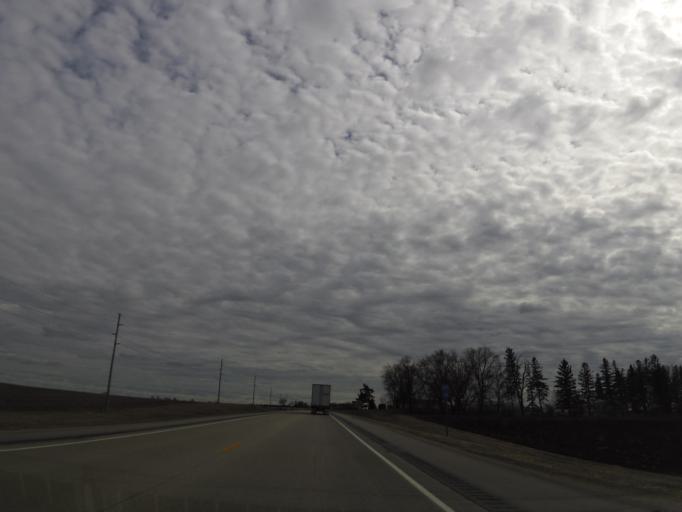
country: US
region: Minnesota
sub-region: Fillmore County
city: Spring Valley
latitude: 43.6071
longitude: -92.3894
